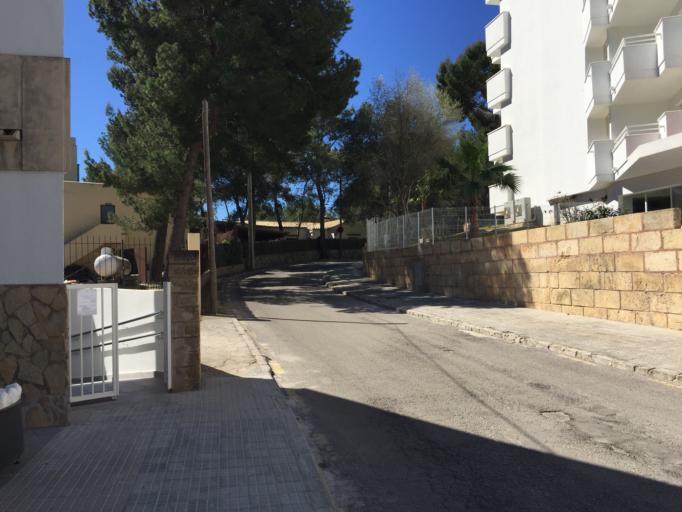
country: ES
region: Balearic Islands
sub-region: Illes Balears
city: Camp de Mar
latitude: 39.5409
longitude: 2.4500
